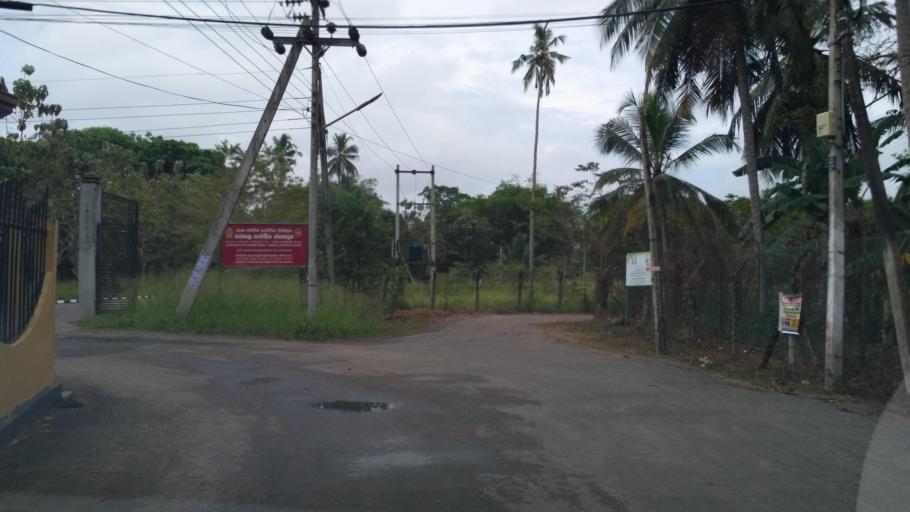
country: LK
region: North Western
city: Kuliyapitiya
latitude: 7.3266
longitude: 80.0215
